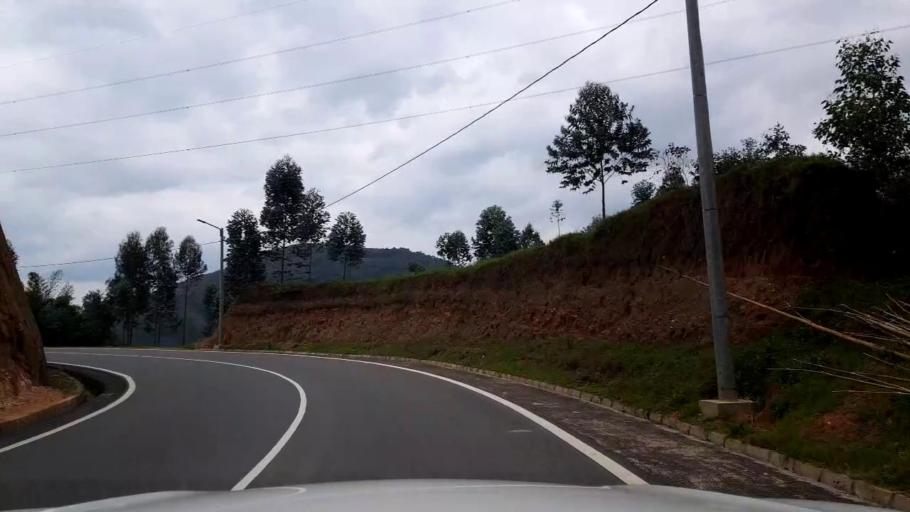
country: RW
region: Western Province
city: Kibuye
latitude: -1.9270
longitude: 29.3731
